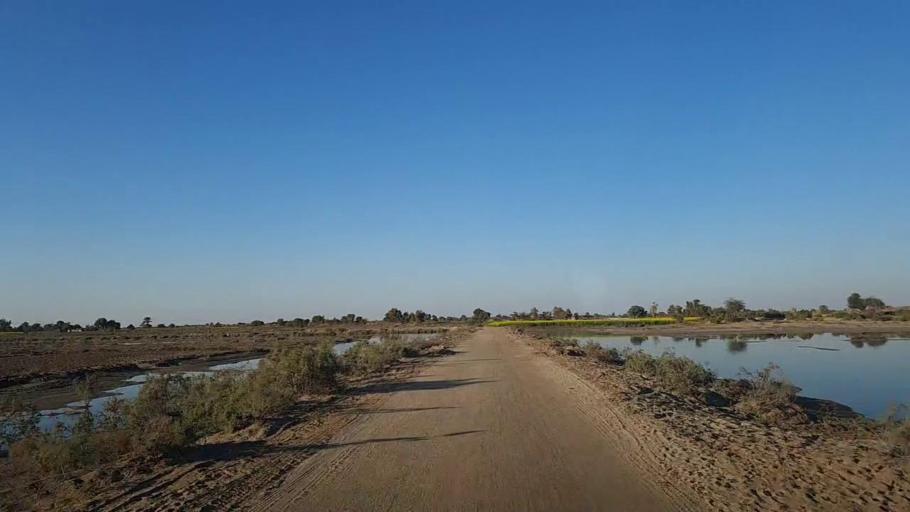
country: PK
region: Sindh
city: Sanghar
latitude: 26.1462
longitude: 68.9265
